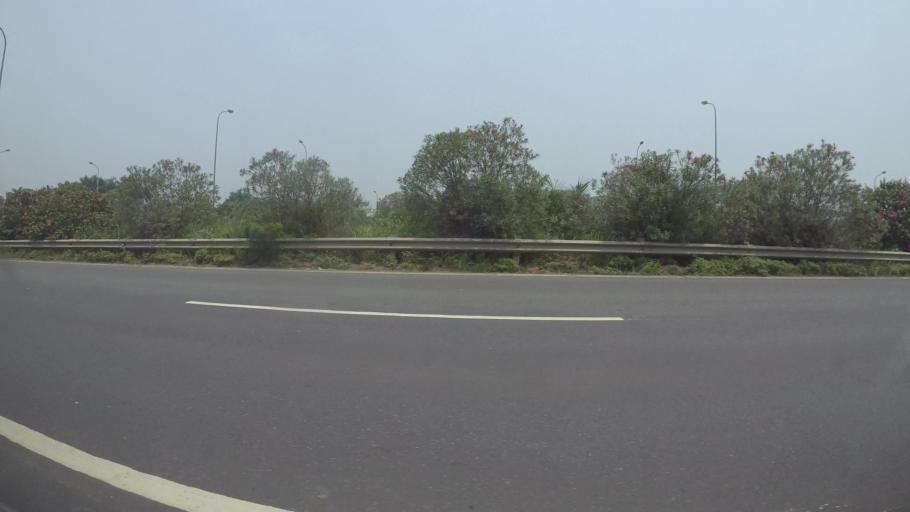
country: VN
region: Ha Noi
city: Quoc Oai
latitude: 21.0009
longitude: 105.6062
